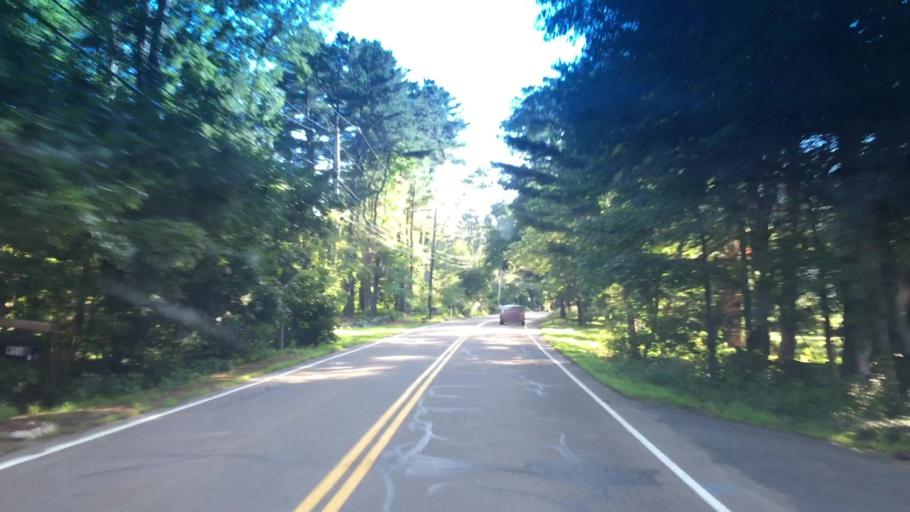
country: US
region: Massachusetts
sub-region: Norfolk County
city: Norfolk
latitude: 42.1319
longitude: -71.2891
